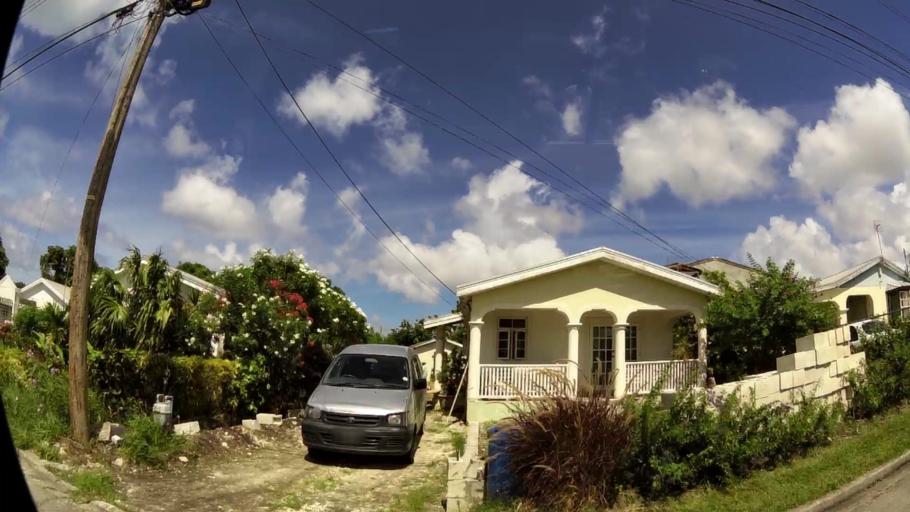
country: BB
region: Saint James
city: Holetown
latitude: 13.1477
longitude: -59.6292
